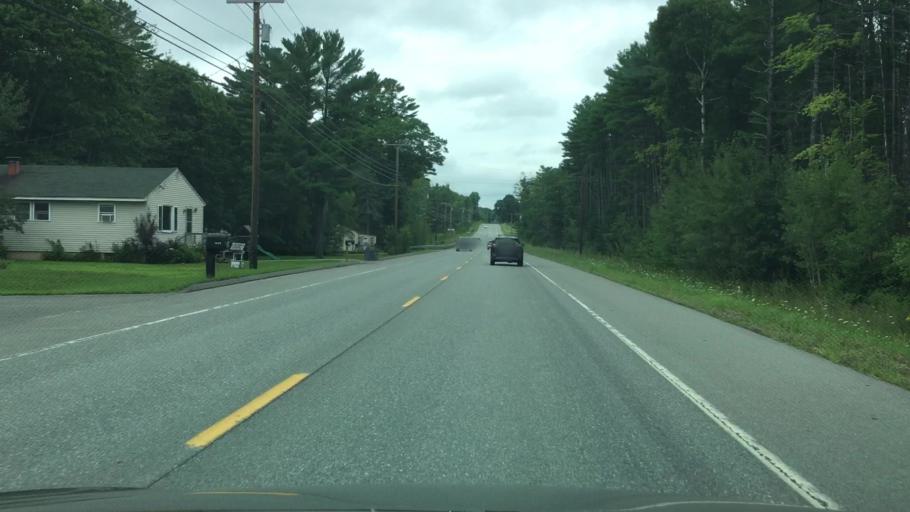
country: US
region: Maine
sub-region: Penobscot County
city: Orrington
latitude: 44.7065
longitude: -68.8237
